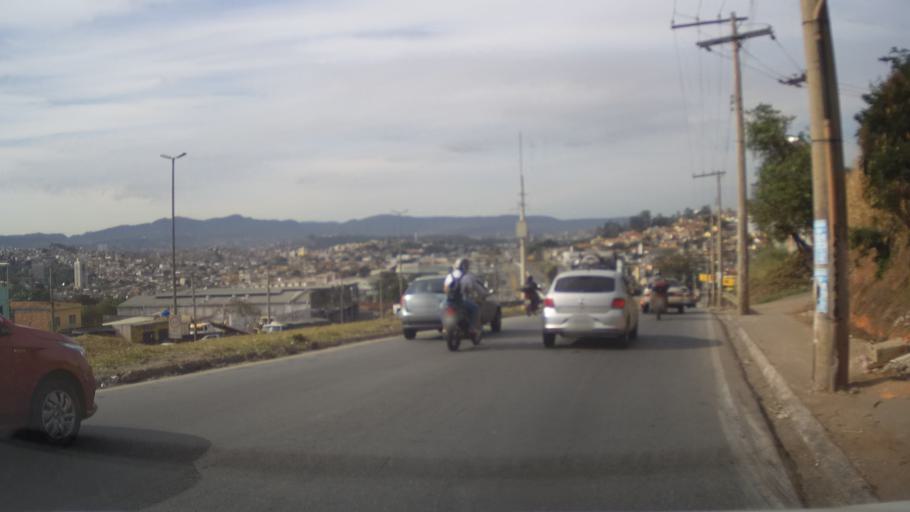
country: BR
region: Minas Gerais
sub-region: Contagem
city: Contagem
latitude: -19.9278
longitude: -44.0069
